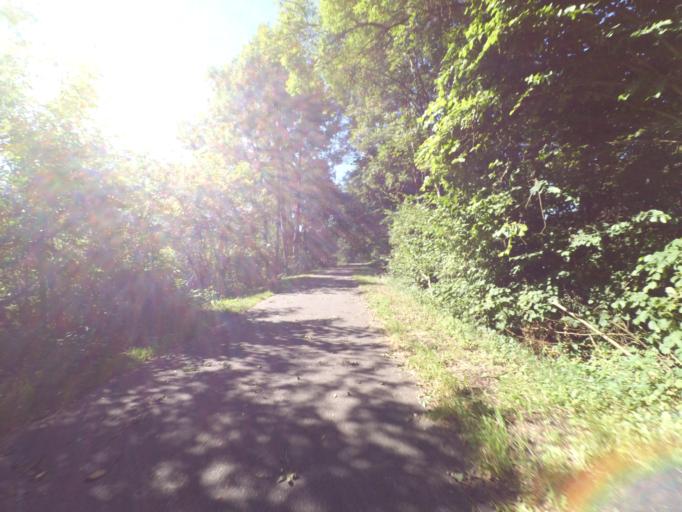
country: DE
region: Rheinland-Pfalz
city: Hasborn
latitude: 50.0456
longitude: 6.9124
